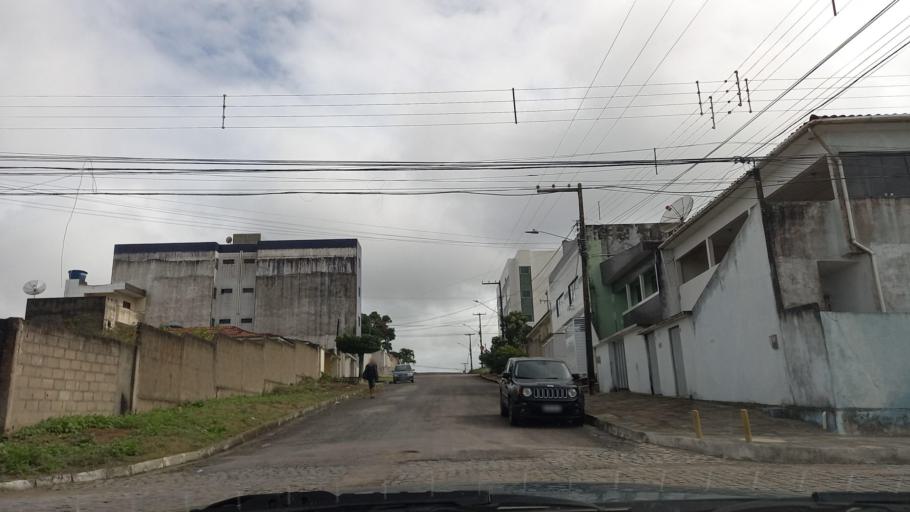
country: BR
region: Pernambuco
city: Garanhuns
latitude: -8.9034
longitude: -36.4905
